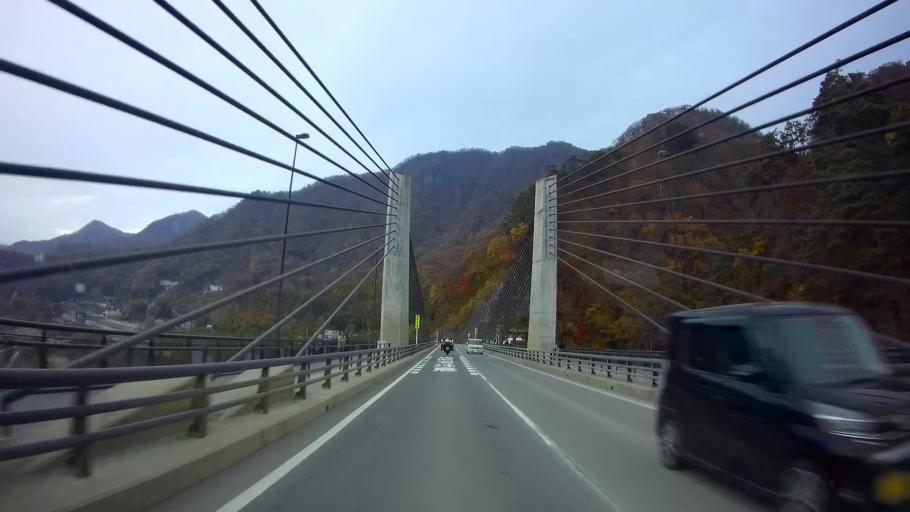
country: JP
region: Gunma
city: Nakanojomachi
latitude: 36.5445
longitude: 138.6889
